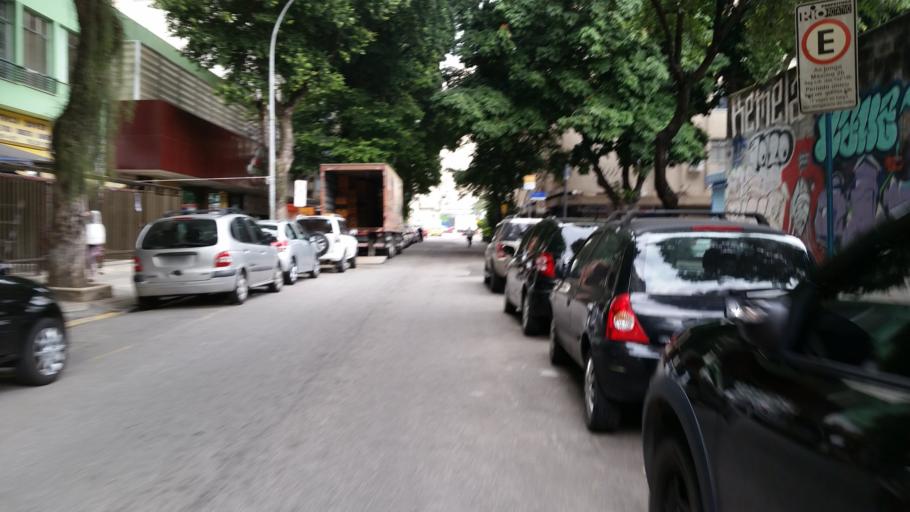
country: BR
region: Rio de Janeiro
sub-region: Rio De Janeiro
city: Rio de Janeiro
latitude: -22.9312
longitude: -43.1764
